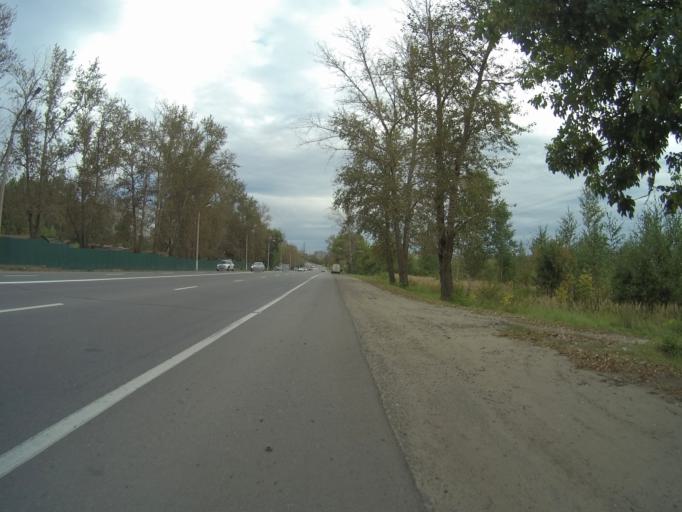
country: RU
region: Vladimir
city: Vladimir
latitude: 56.1272
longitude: 40.3450
